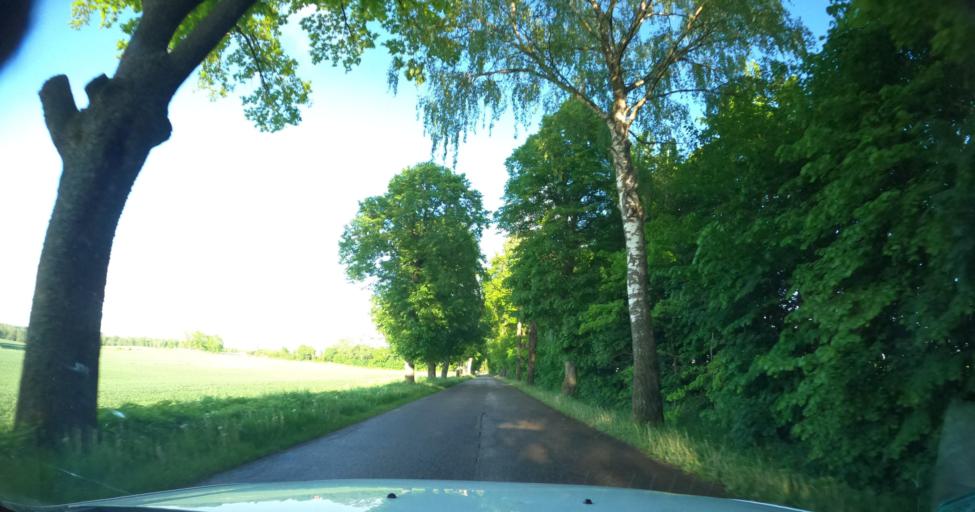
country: PL
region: Warmian-Masurian Voivodeship
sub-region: Powiat braniewski
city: Pieniezno
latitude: 54.2546
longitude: 19.9752
